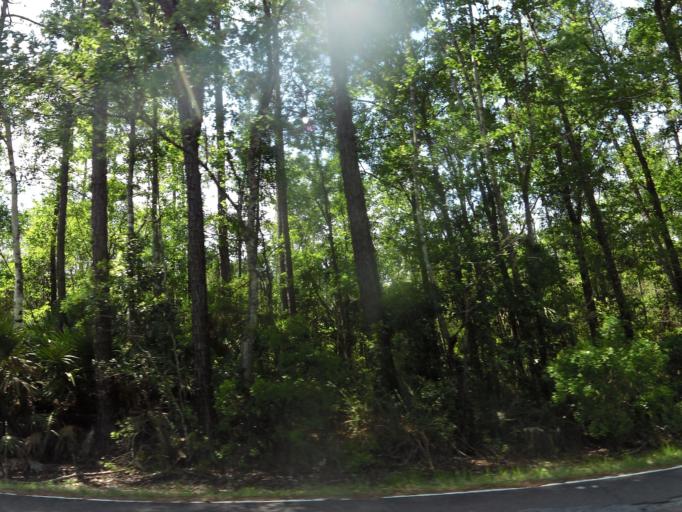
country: US
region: Florida
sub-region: Nassau County
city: Yulee
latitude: 30.5148
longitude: -81.6603
